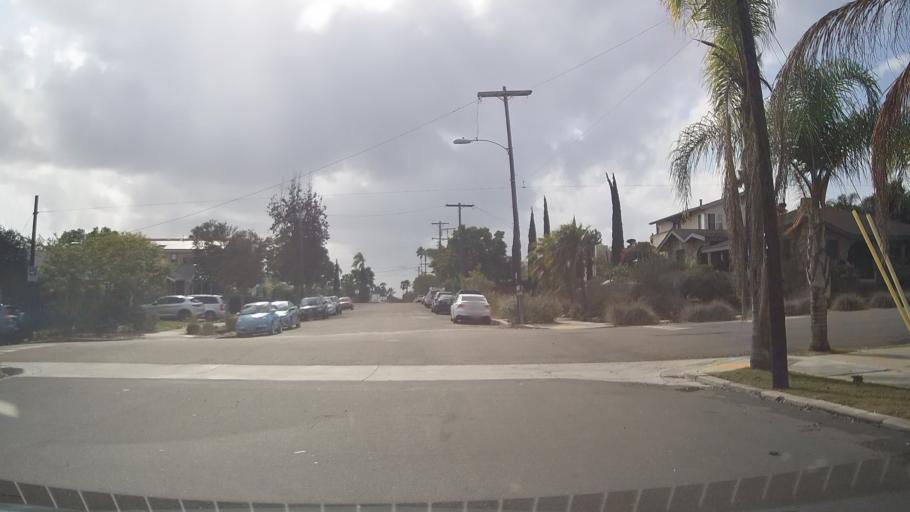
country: US
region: California
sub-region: San Diego County
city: San Diego
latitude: 32.7309
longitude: -117.1244
